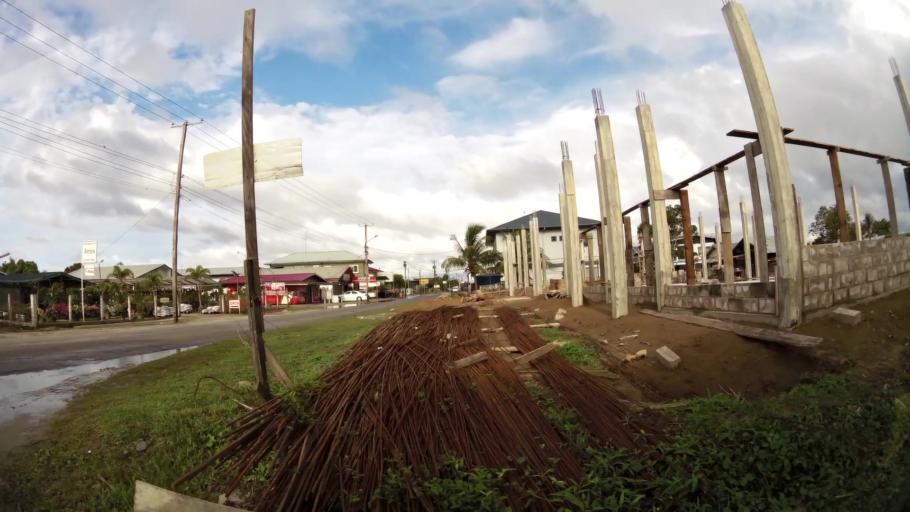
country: SR
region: Paramaribo
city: Paramaribo
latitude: 5.8476
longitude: -55.2408
